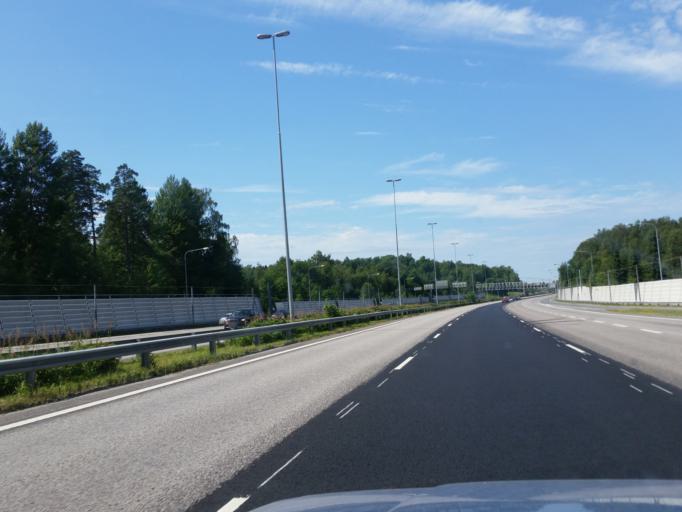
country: FI
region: Uusimaa
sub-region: Helsinki
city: Otaniemi
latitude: 60.1690
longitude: 24.7973
